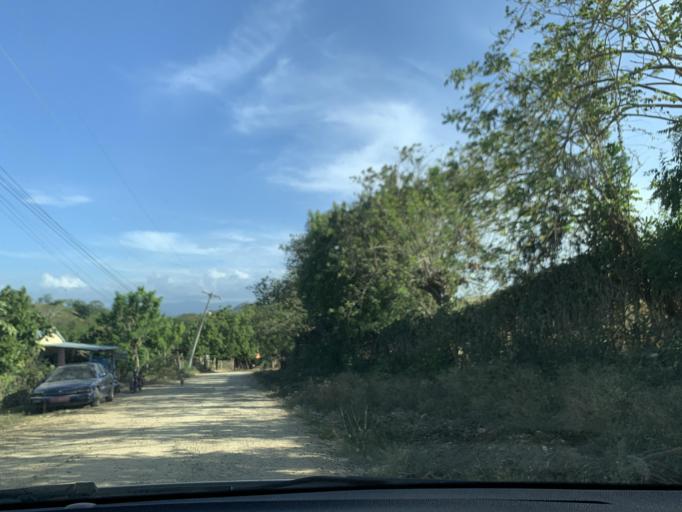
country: DO
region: Puerto Plata
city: Luperon
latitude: 19.8719
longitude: -70.9403
